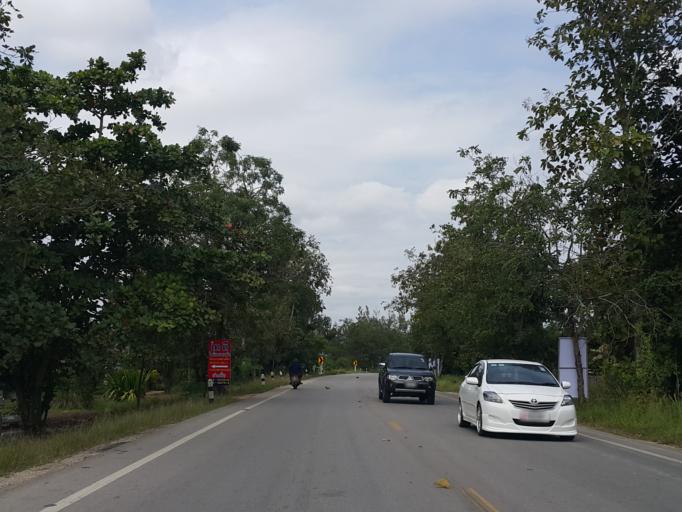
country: TH
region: Lampang
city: Lampang
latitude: 18.3315
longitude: 99.4624
